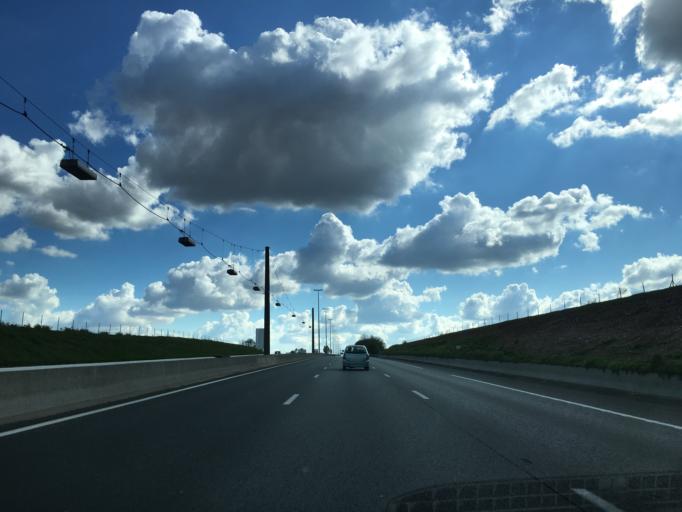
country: FR
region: Nord-Pas-de-Calais
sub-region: Departement du Pas-de-Calais
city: Fampoux
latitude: 50.2853
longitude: 2.8783
